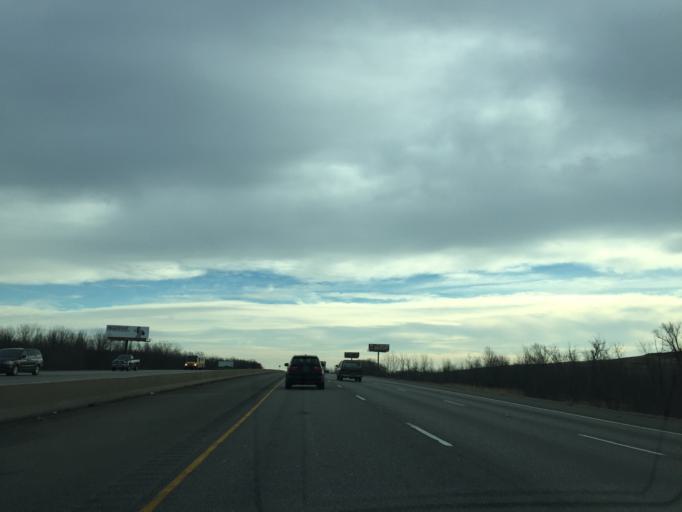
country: US
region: Indiana
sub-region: LaPorte County
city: Michigan City
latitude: 41.6583
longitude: -86.9118
